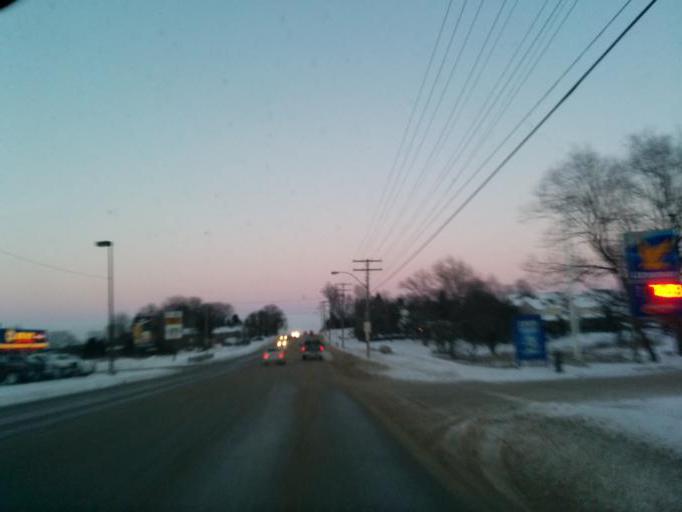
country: CA
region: Ontario
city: Shelburne
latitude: 44.0801
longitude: -80.1958
